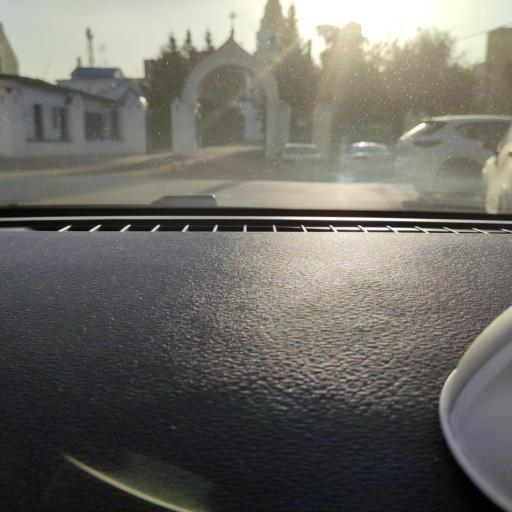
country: RU
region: Samara
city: Samara
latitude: 53.1866
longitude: 50.1058
